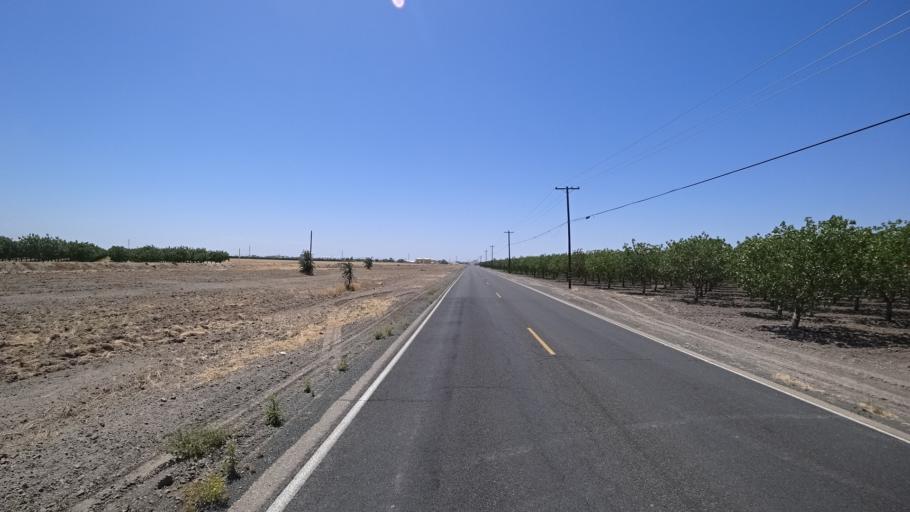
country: US
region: California
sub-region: Kings County
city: Corcoran
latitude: 36.1149
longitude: -119.5451
